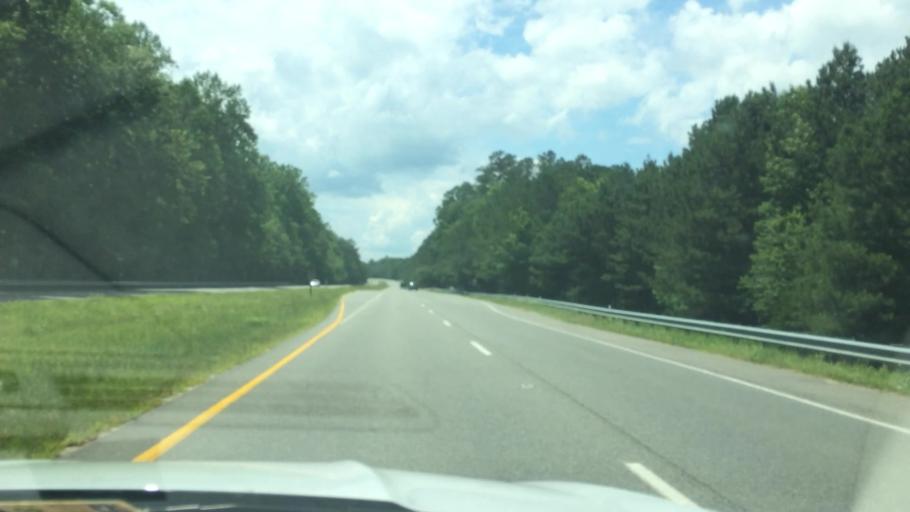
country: US
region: Virginia
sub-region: Middlesex County
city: Saluda
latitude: 37.5639
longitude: -76.6386
